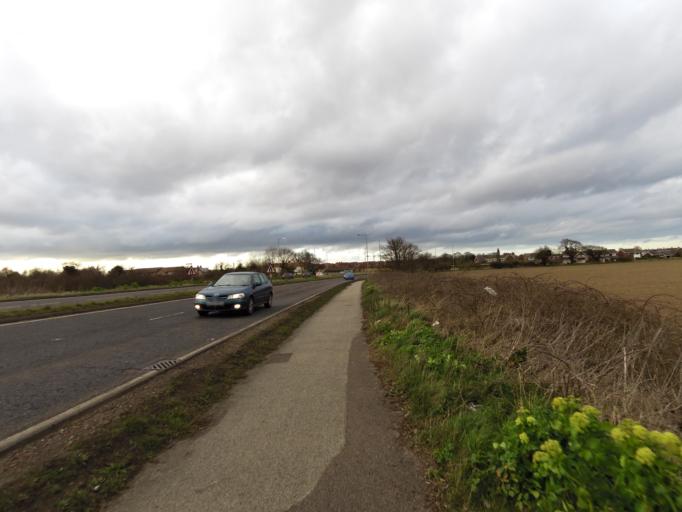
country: GB
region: England
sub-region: Norfolk
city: Gorleston-on-Sea
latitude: 52.5546
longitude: 1.7176
